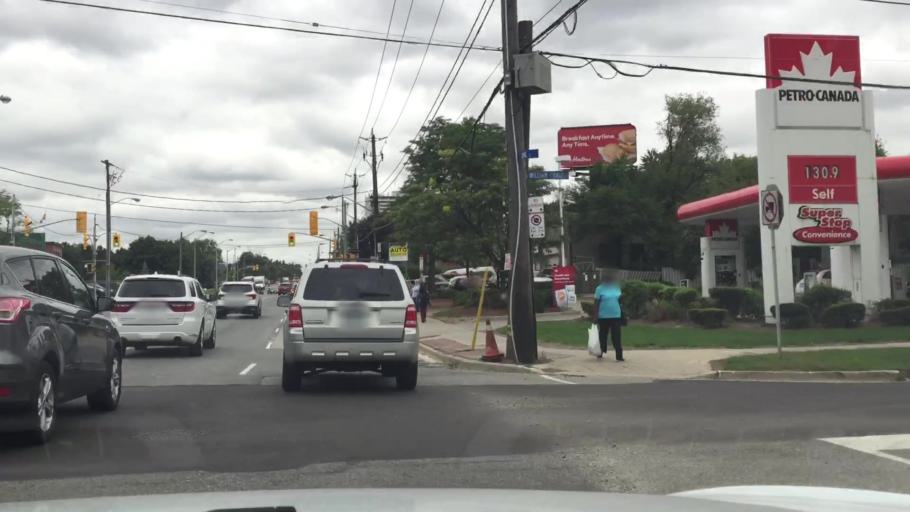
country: CA
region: Ontario
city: Concord
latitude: 43.7223
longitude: -79.5089
